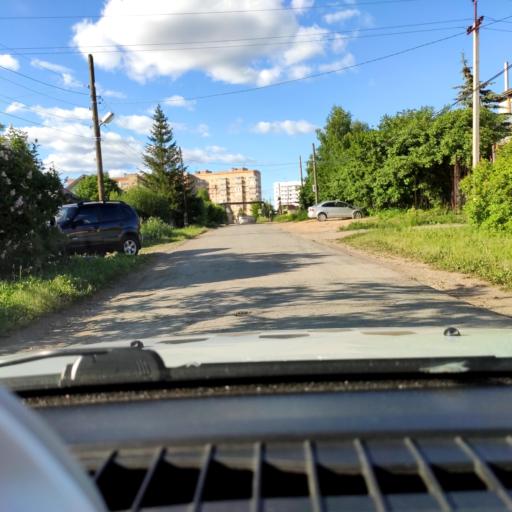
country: RU
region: Perm
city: Froly
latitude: 57.9180
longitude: 56.2759
